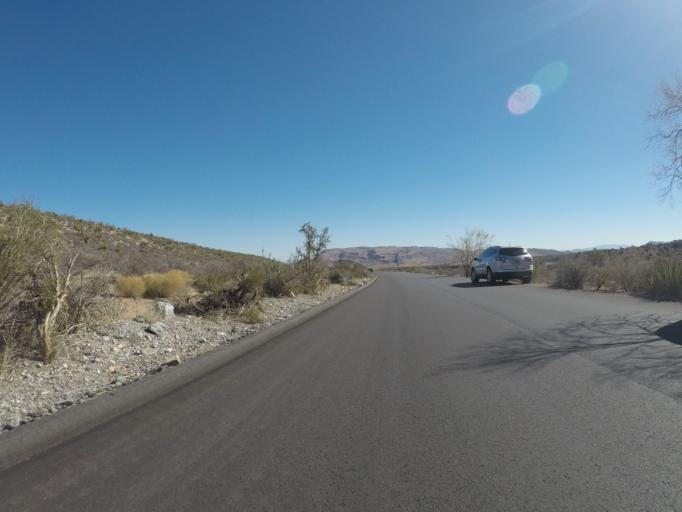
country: US
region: Nevada
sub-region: Clark County
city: Summerlin South
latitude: 36.1483
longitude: -115.4809
